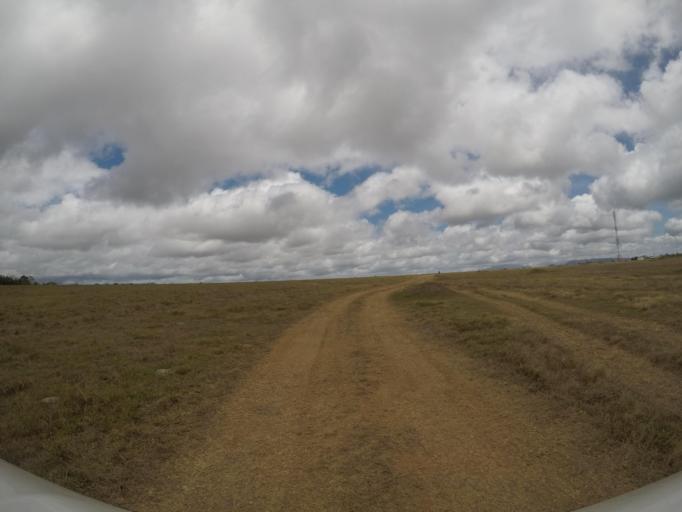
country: TL
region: Lautem
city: Lospalos
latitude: -8.4426
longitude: 126.9909
